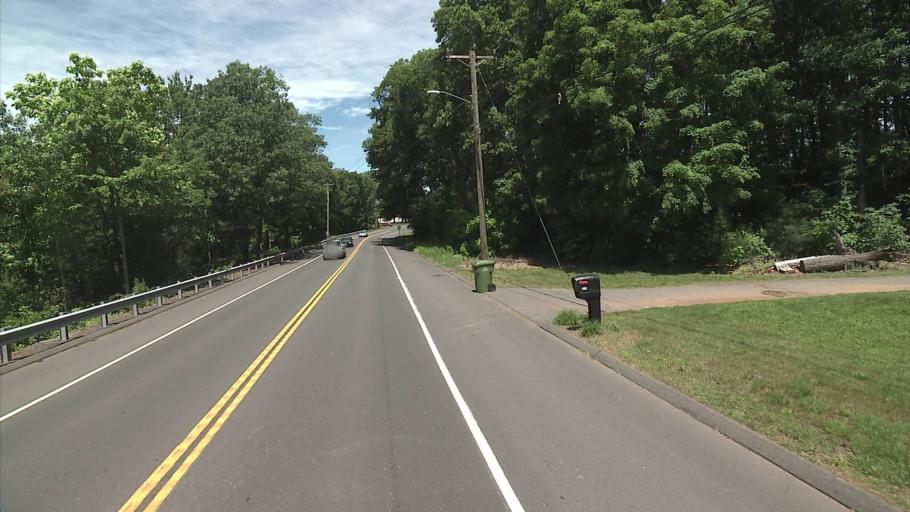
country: US
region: Connecticut
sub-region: New Haven County
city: Meriden
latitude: 41.5801
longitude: -72.8681
